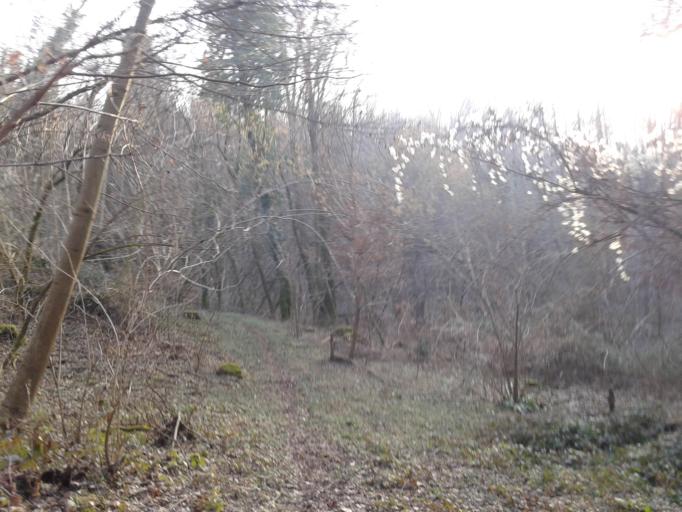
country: IT
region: Veneto
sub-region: Provincia di Vicenza
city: Monte di Malo
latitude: 45.6680
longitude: 11.3661
